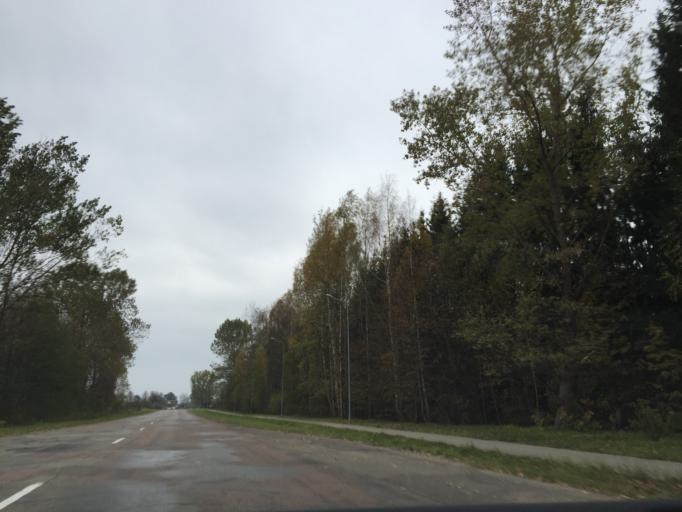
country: LV
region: Marupe
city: Marupe
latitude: 56.8492
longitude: 24.0503
